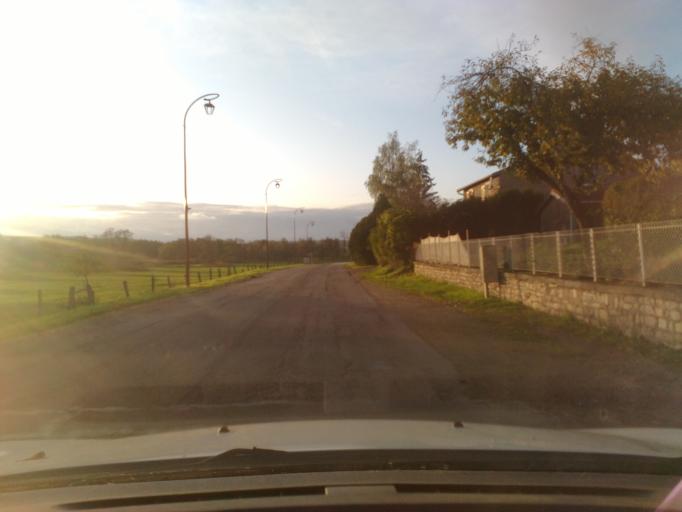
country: FR
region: Lorraine
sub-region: Departement des Vosges
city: Mirecourt
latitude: 48.2579
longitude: 6.1856
